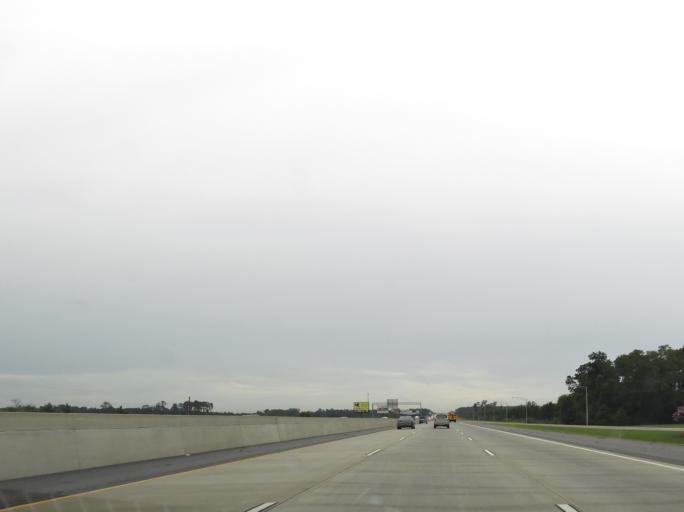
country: US
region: Georgia
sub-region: Cook County
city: Sparks
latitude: 31.2610
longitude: -83.4704
